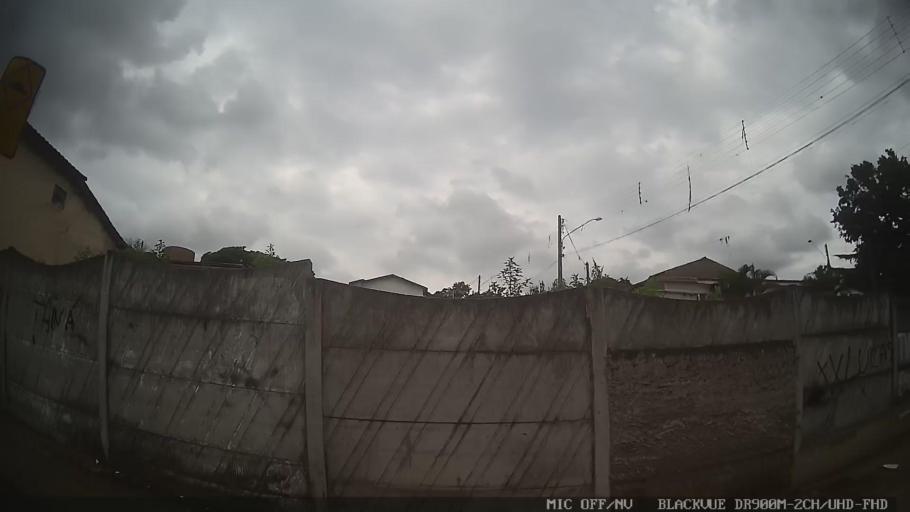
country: BR
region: Sao Paulo
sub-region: Atibaia
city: Atibaia
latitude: -23.1181
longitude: -46.5858
